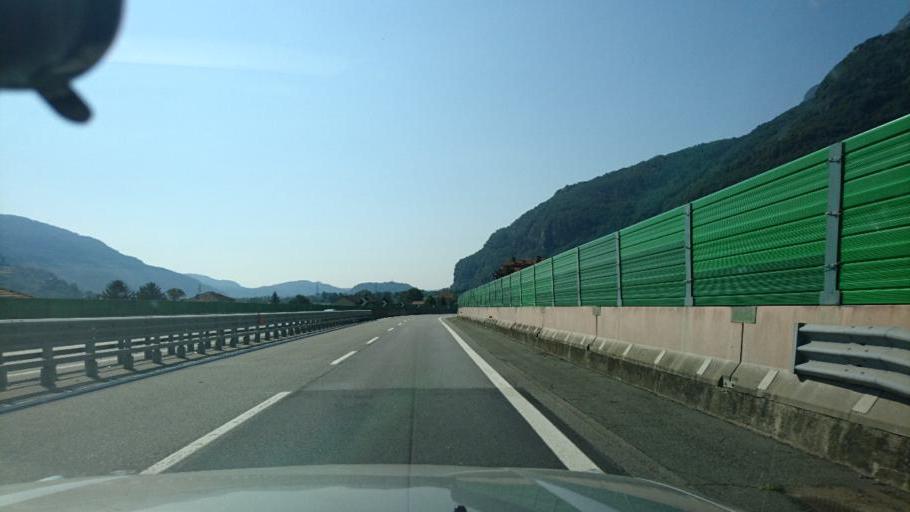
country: IT
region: Piedmont
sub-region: Provincia di Torino
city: Tavagnasco
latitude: 45.5480
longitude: 7.8232
